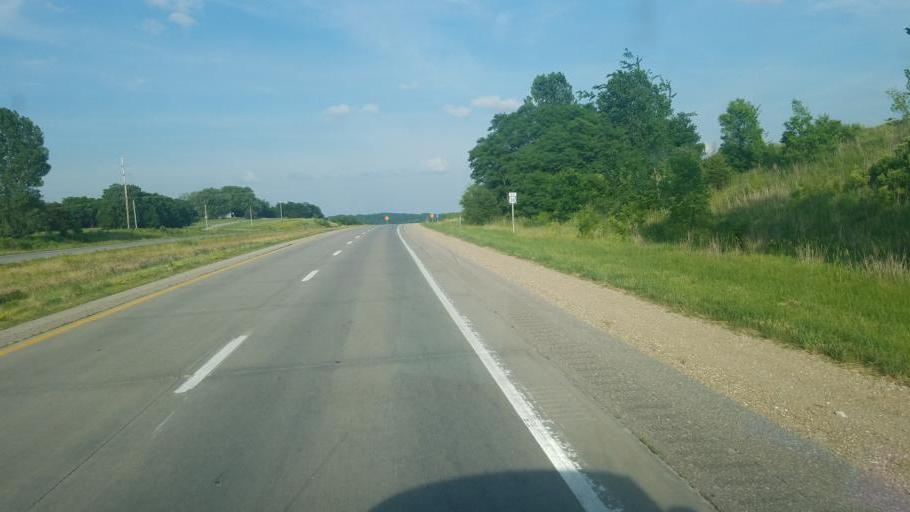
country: US
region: Iowa
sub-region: Tama County
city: Toledo
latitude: 42.0060
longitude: -92.7390
